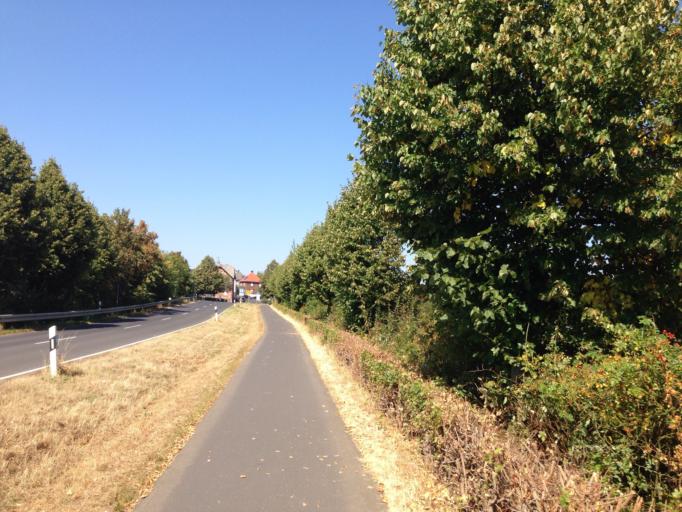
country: DE
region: Hesse
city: Lollar
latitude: 50.6309
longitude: 8.6810
